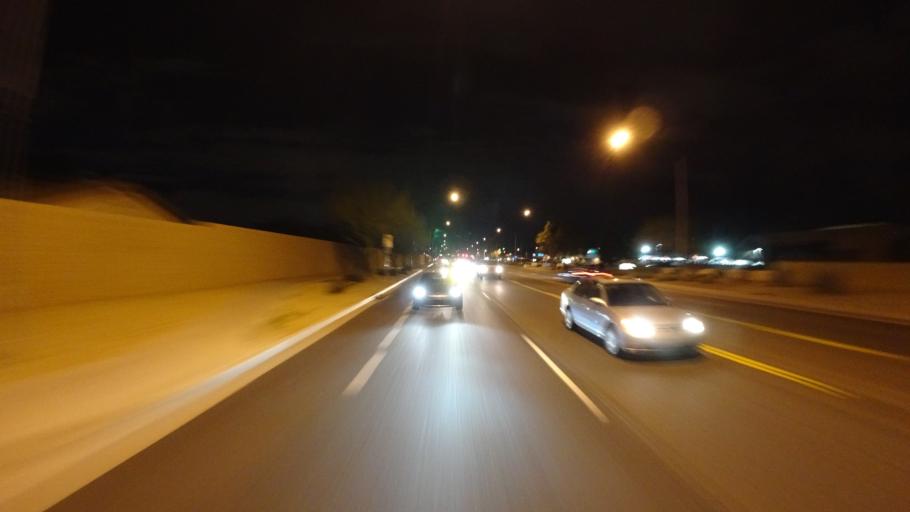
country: US
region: Arizona
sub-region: Maricopa County
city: San Carlos
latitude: 33.3606
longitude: -111.8767
